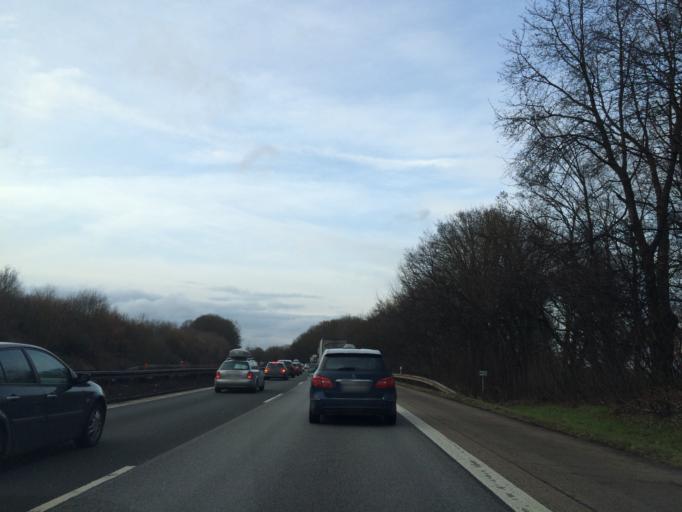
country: DE
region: Bavaria
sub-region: Regierungsbezirk Unterfranken
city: Marktheidenfeld
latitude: 49.8045
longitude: 9.5861
